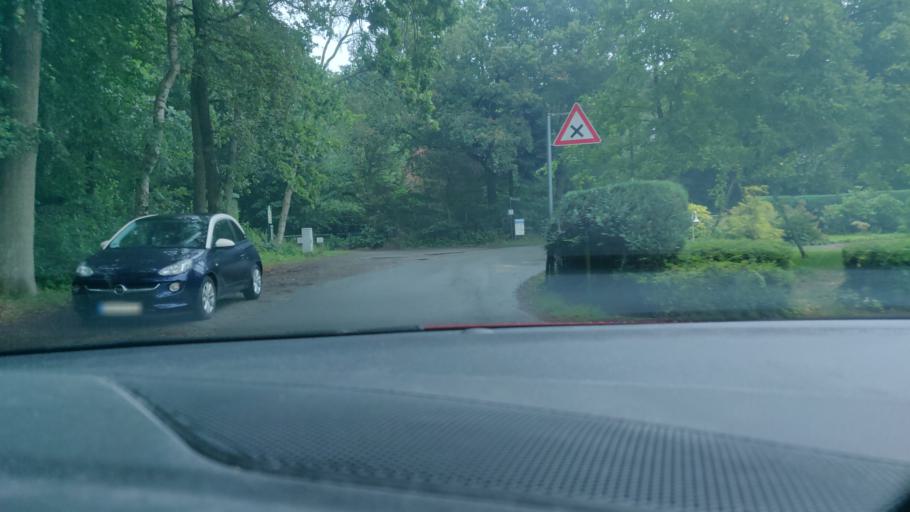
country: DE
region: Lower Saxony
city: Nordholz
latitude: 53.8638
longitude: 8.6064
